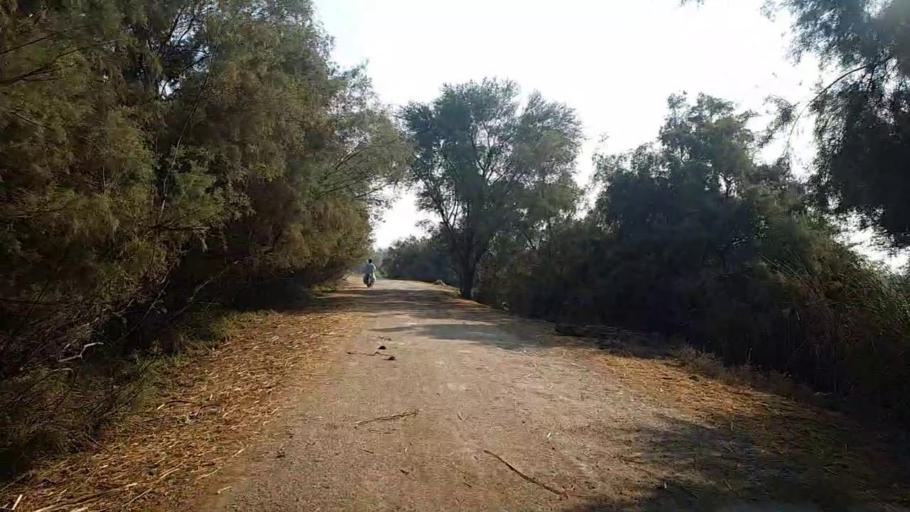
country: PK
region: Sindh
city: Mirpur Mathelo
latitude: 27.8955
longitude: 69.6071
